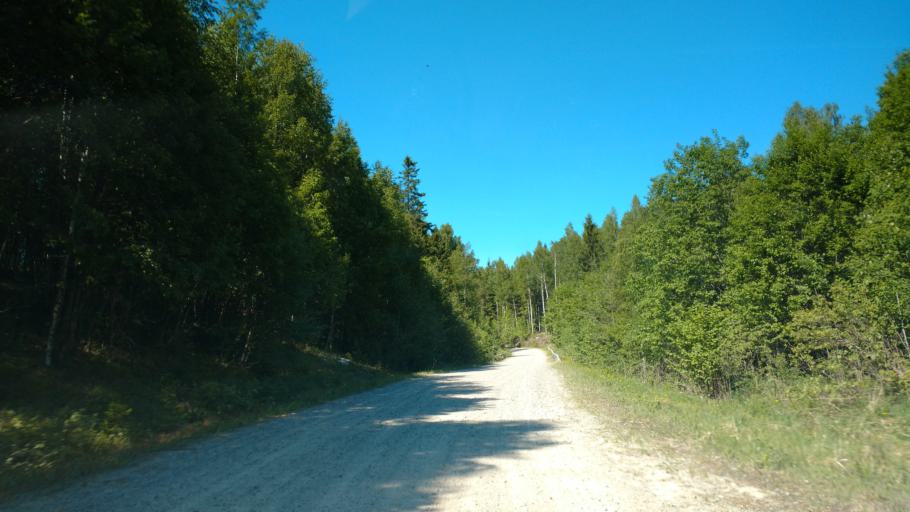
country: FI
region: Varsinais-Suomi
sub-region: Salo
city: Halikko
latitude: 60.4263
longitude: 22.9605
